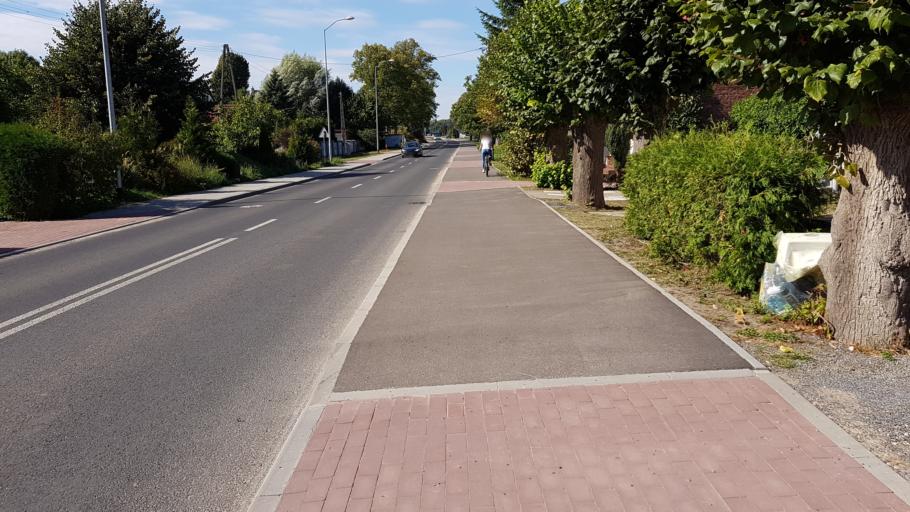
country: PL
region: West Pomeranian Voivodeship
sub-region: Powiat policki
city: Przeclaw
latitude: 53.3487
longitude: 14.4775
